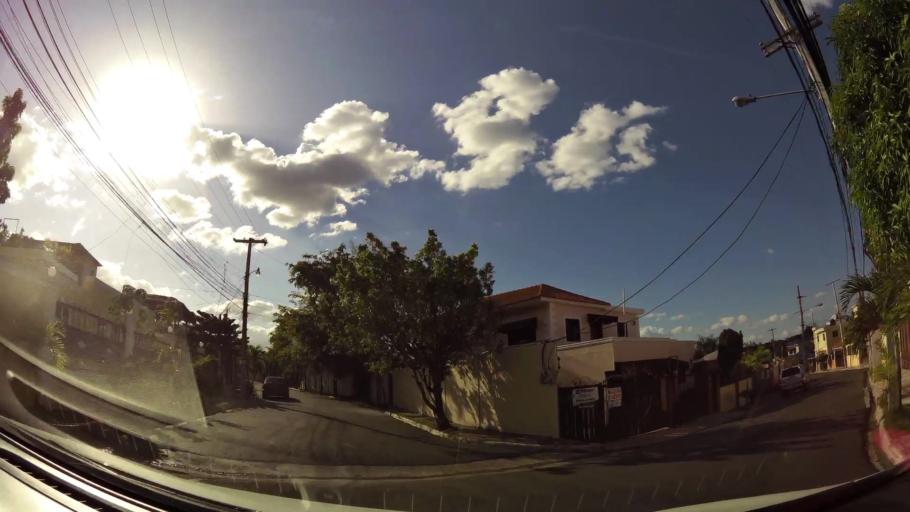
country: DO
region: Nacional
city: Santo Domingo
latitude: 18.5091
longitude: -69.9770
